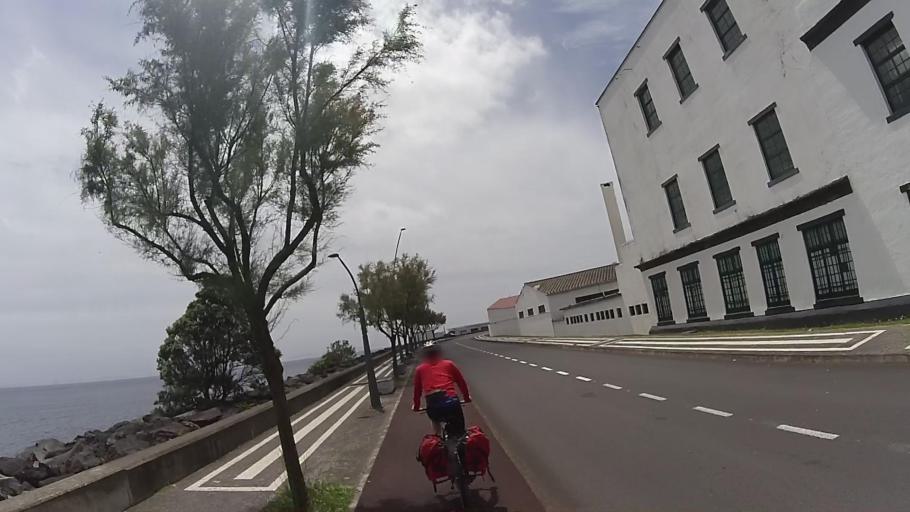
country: PT
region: Azores
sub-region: Ponta Delgada
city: Rosto de Cao
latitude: 37.7438
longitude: -25.6488
